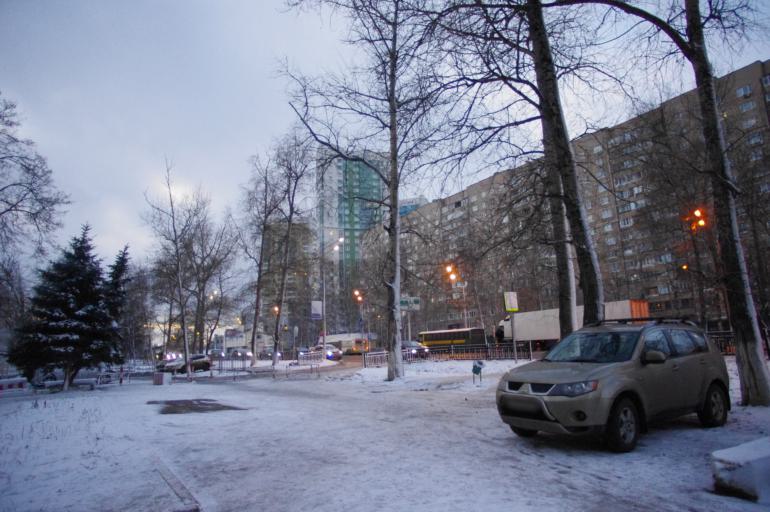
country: RU
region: Moskovskaya
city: Krasnogorsk
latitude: 55.8049
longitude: 37.3268
